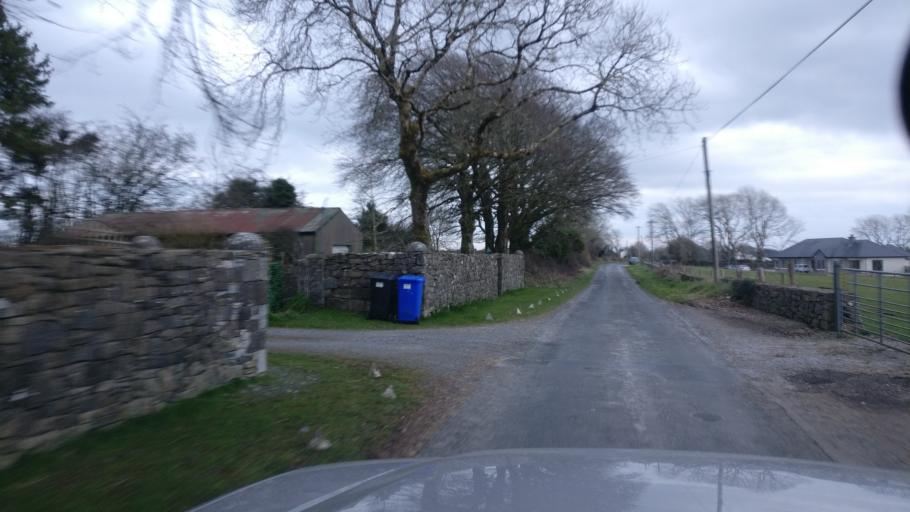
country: IE
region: Connaught
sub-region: County Galway
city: Loughrea
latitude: 53.2660
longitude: -8.4667
